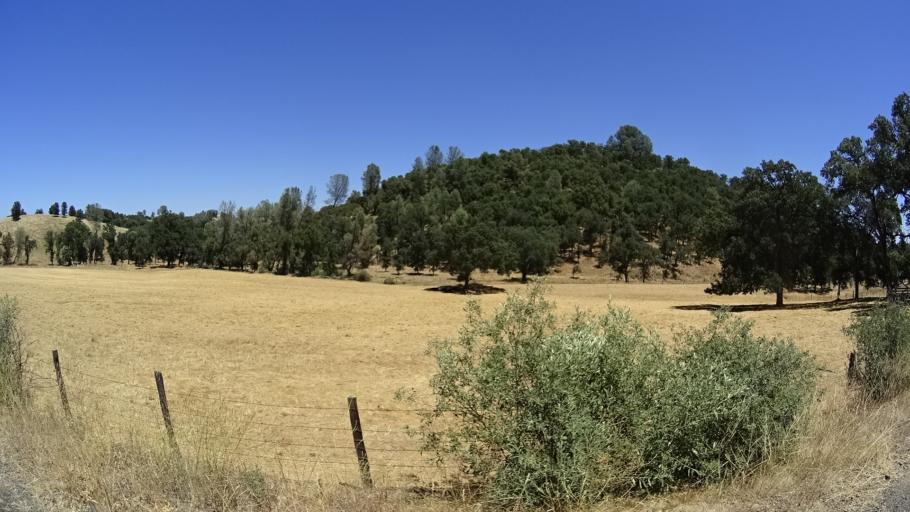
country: US
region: California
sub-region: Calaveras County
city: San Andreas
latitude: 38.1118
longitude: -120.6575
